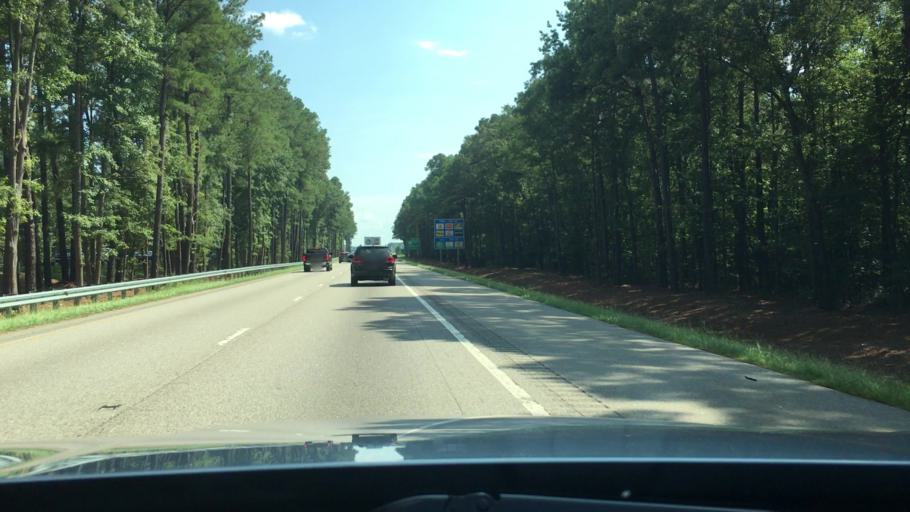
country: US
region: North Carolina
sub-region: Robeson County
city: Lumberton
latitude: 34.6832
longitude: -79.0019
